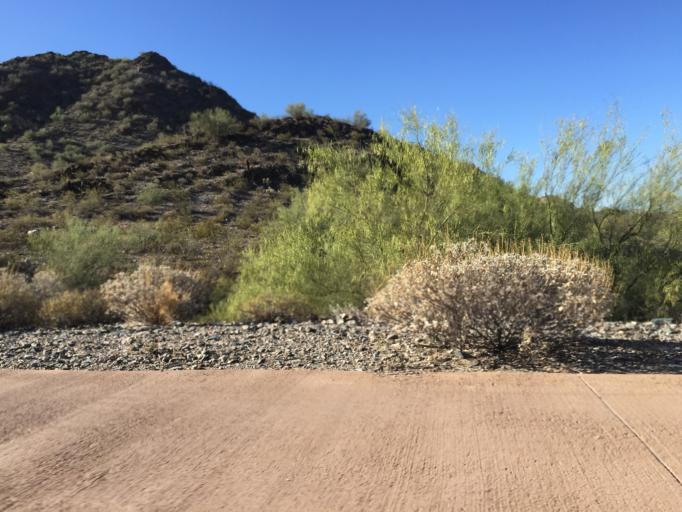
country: US
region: Arizona
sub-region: Maricopa County
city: Paradise Valley
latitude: 33.5600
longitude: -112.0344
